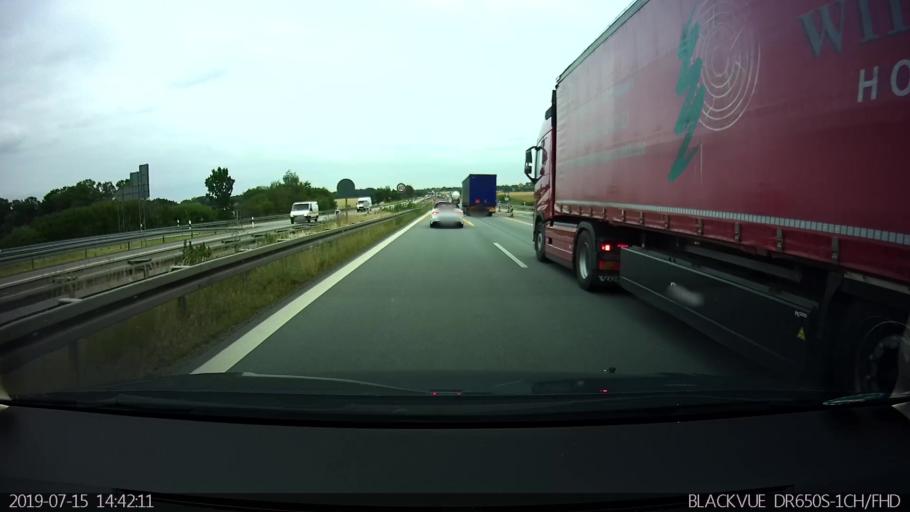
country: DE
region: Saxony
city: Panschwitz-Kuckau
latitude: 51.1982
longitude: 14.2244
